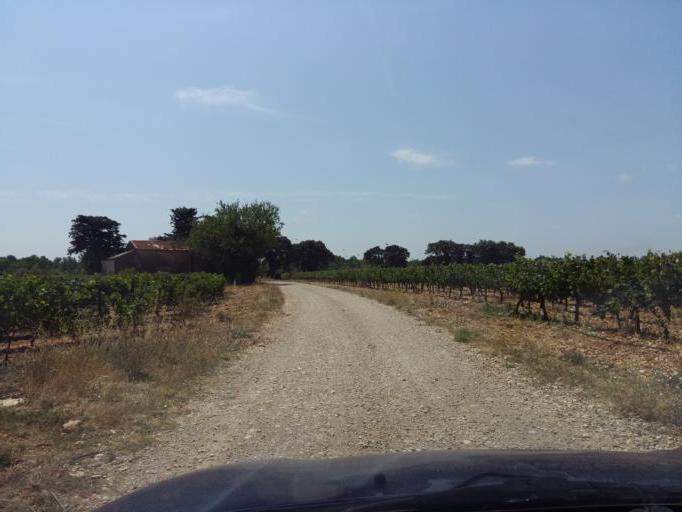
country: FR
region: Provence-Alpes-Cote d'Azur
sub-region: Departement du Vaucluse
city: Camaret-sur-Aigues
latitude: 44.1782
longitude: 4.8715
